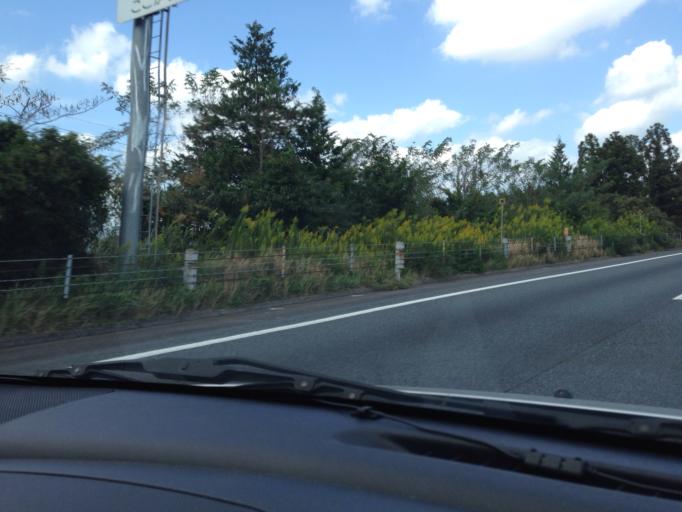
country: JP
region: Ibaraki
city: Ishioka
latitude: 36.2526
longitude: 140.2971
